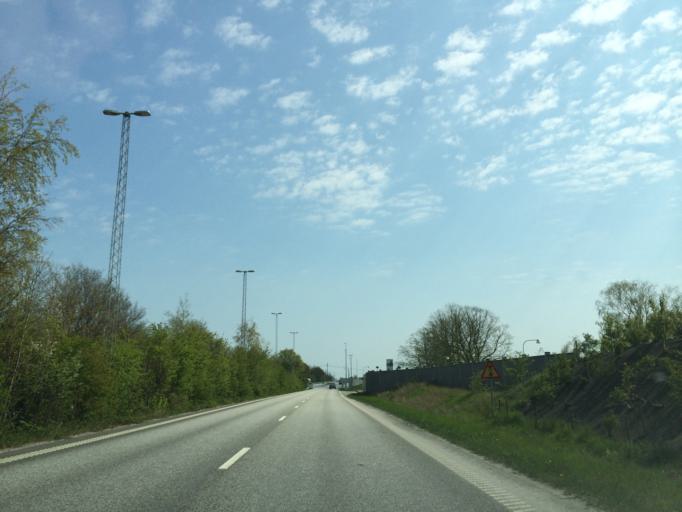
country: SE
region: Skane
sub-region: Lunds Kommun
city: Lund
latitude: 55.6933
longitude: 13.2373
